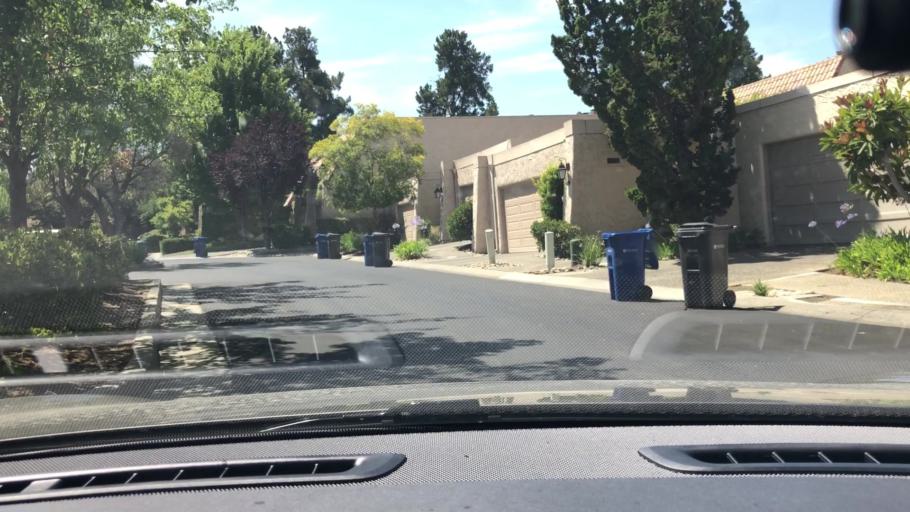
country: US
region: California
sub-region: Santa Clara County
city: Monte Sereno
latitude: 37.2617
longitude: -121.9888
